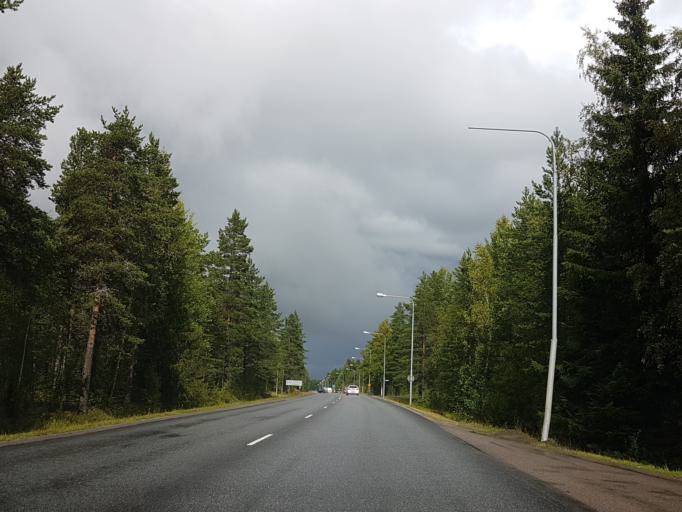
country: SE
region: Vaesterbotten
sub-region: Umea Kommun
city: Ersmark
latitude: 63.8501
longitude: 20.3431
